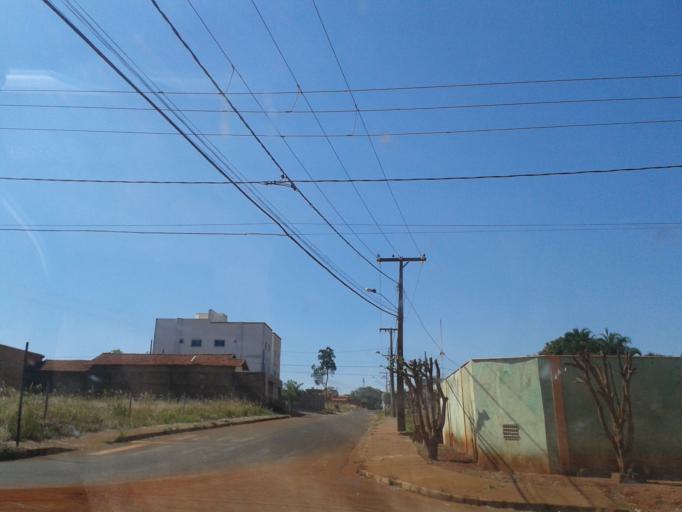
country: BR
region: Minas Gerais
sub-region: Ituiutaba
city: Ituiutaba
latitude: -18.9973
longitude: -49.4586
